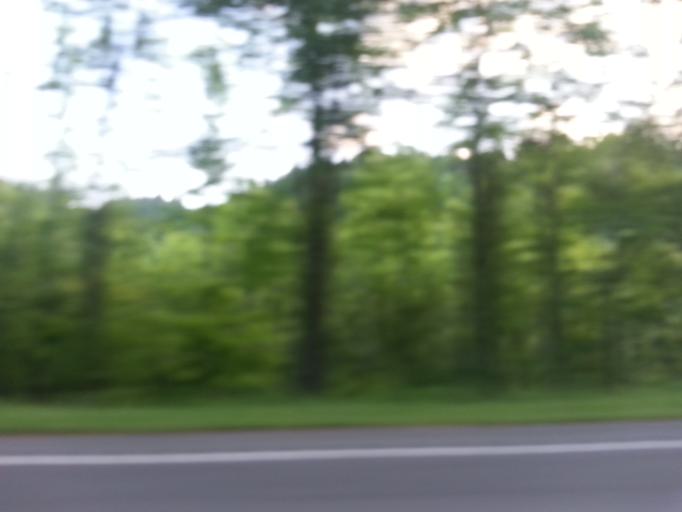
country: US
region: Georgia
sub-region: Fannin County
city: McCaysville
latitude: 35.1693
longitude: -84.3212
